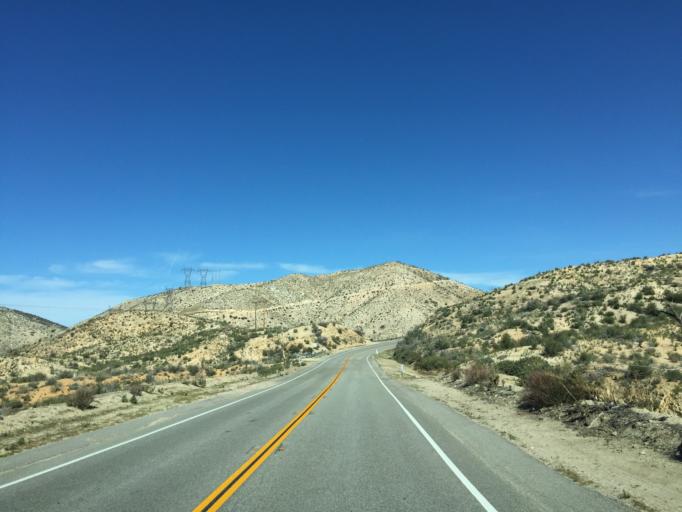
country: US
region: California
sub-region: Los Angeles County
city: Vincent
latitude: 34.4277
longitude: -118.0907
